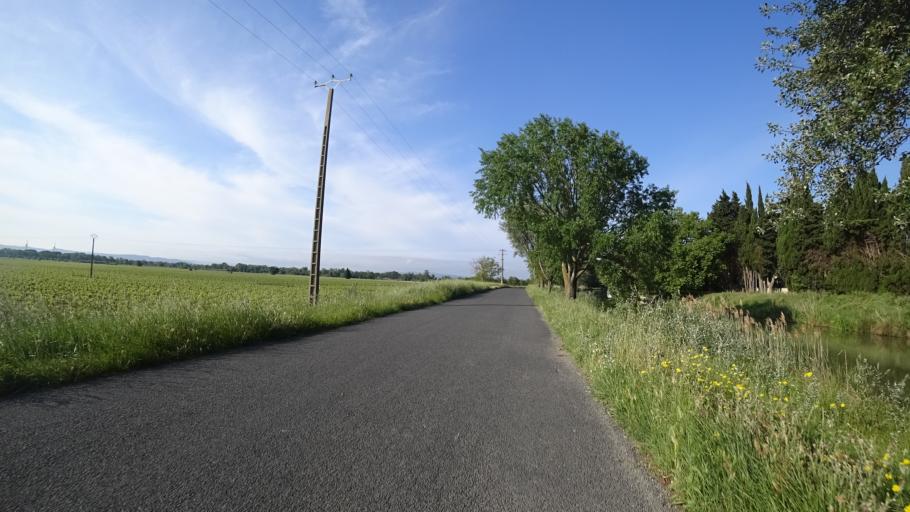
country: FR
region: Languedoc-Roussillon
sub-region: Departement de l'Aude
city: Canet
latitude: 43.2449
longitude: 2.8015
